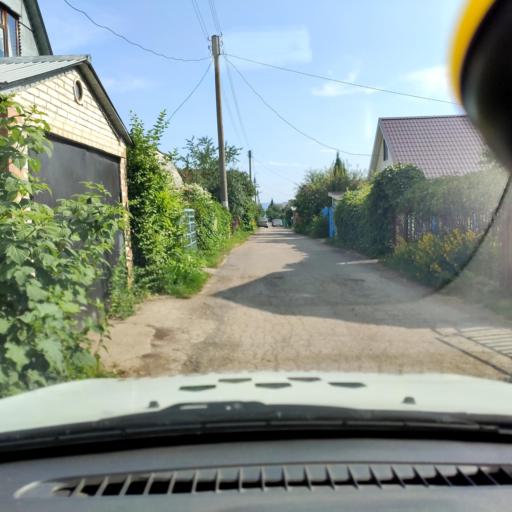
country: RU
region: Samara
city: Podstepki
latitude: 53.5069
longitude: 49.1441
